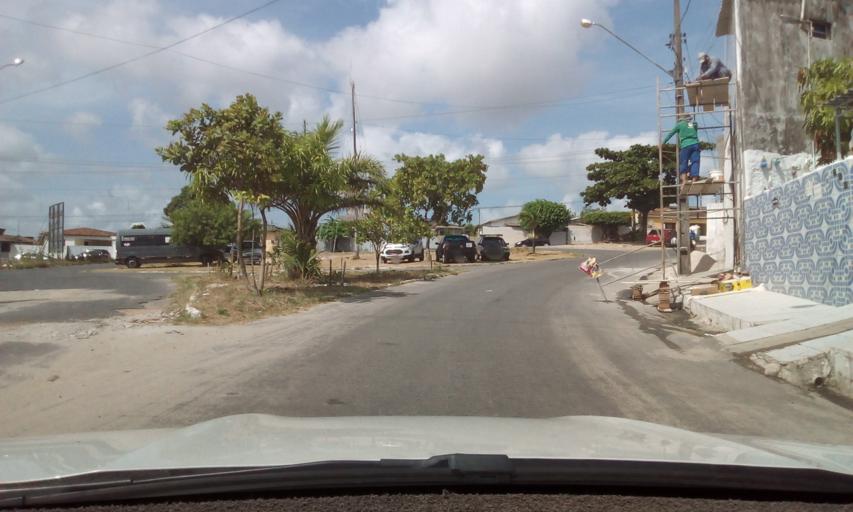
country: BR
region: Paraiba
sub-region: Joao Pessoa
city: Joao Pessoa
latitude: -7.1803
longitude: -34.8842
